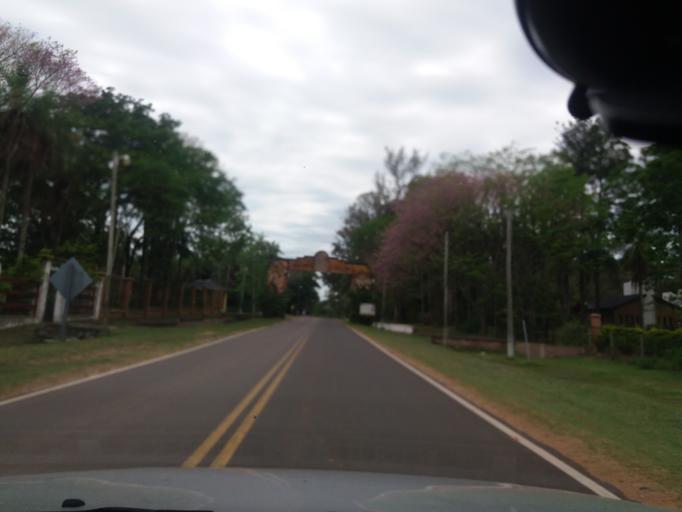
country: AR
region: Corrientes
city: San Luis del Palmar
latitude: -27.4602
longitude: -58.6651
